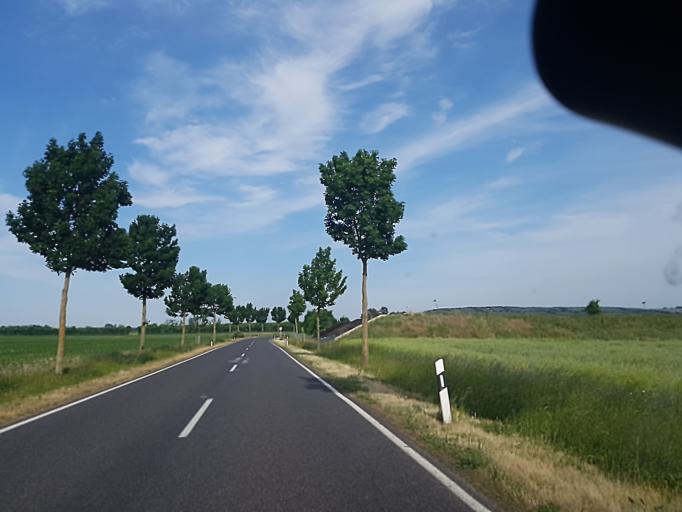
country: DE
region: Saxony-Anhalt
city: Seyda
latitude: 51.8951
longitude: 12.8821
